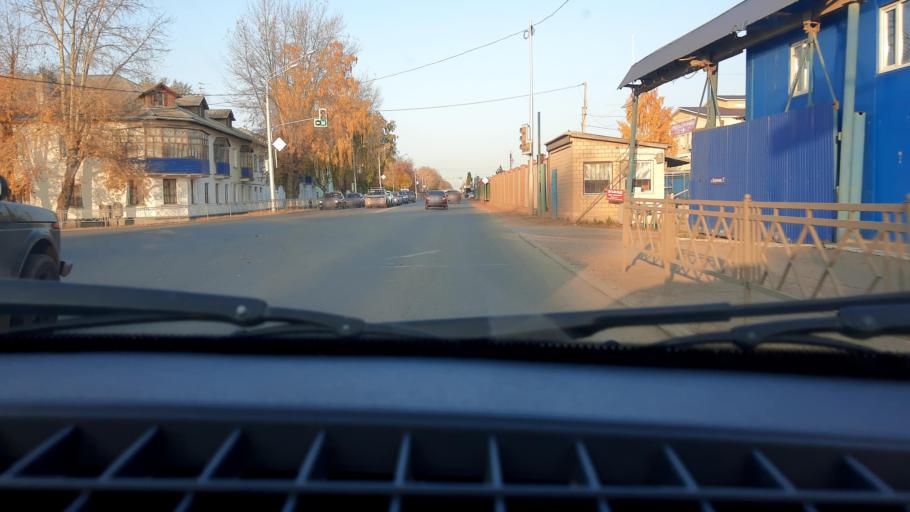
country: RU
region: Bashkortostan
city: Avdon
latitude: 54.6952
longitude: 55.8274
